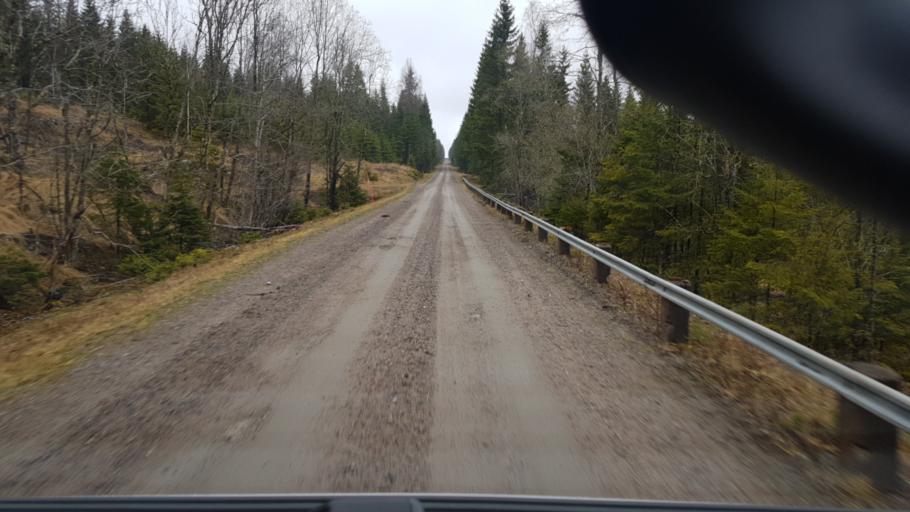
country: SE
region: Vaermland
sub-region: Eda Kommun
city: Charlottenberg
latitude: 59.9994
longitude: 12.5082
